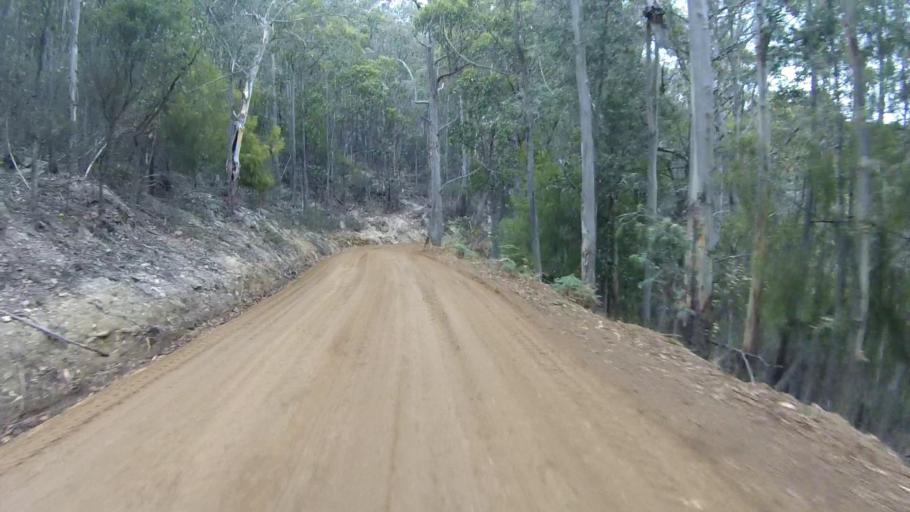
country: AU
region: Tasmania
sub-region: Huon Valley
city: Huonville
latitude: -42.9662
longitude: 147.0467
